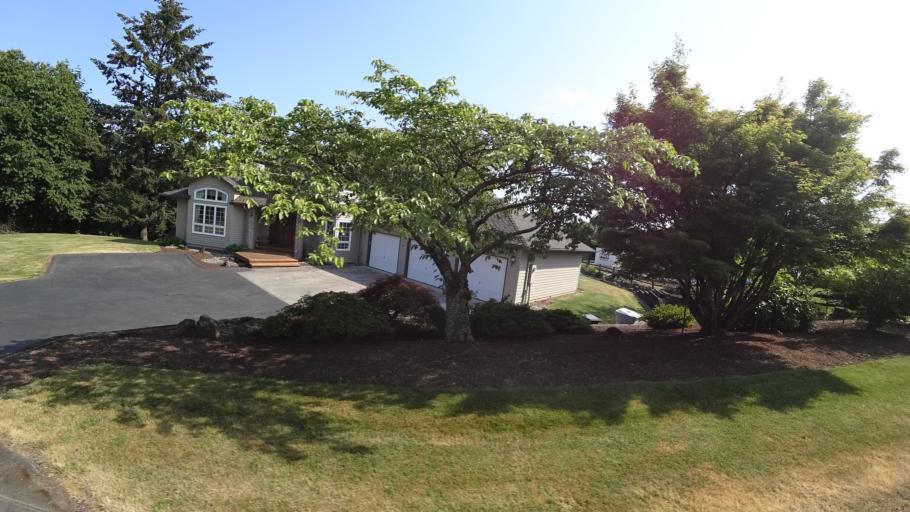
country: US
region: Oregon
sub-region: Clackamas County
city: Happy Valley
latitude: 45.4536
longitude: -122.5362
